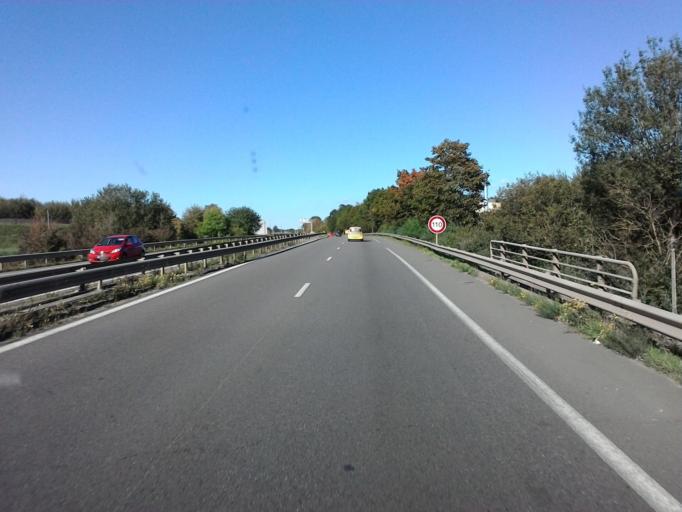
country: FR
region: Lorraine
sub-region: Departement de Meurthe-et-Moselle
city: Longwy
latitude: 49.5219
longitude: 5.7530
